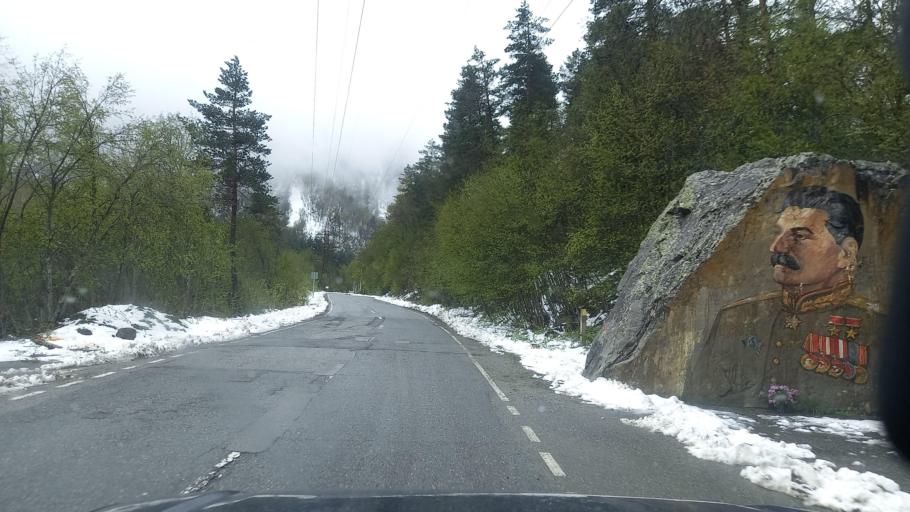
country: RU
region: North Ossetia
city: Mizur
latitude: 42.7974
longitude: 43.9257
